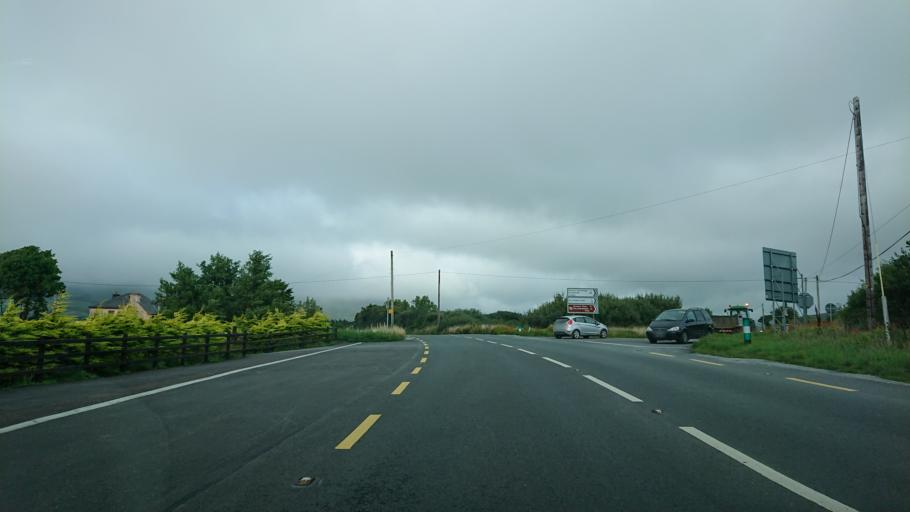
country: IE
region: Munster
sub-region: Ciarrai
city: Cahersiveen
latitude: 51.9529
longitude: -10.1973
